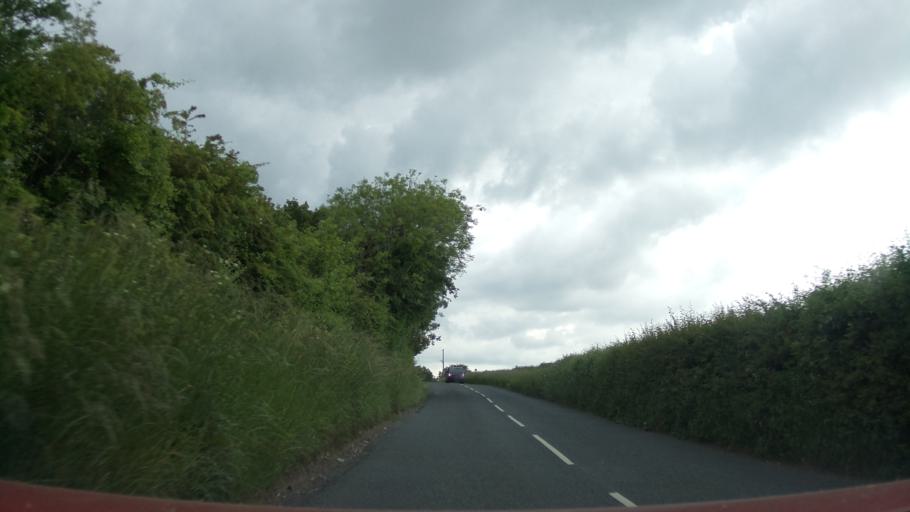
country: GB
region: England
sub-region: South Gloucestershire
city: Pucklechurch
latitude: 51.4777
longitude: -2.4274
